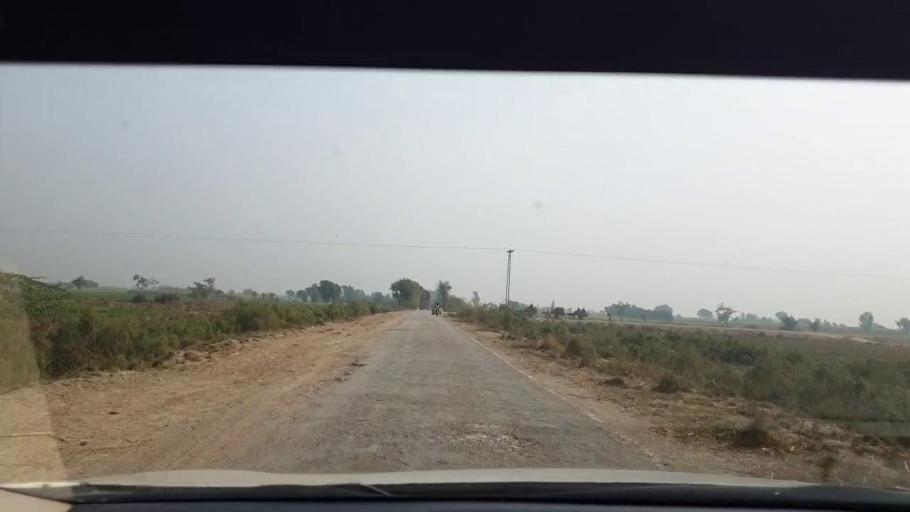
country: PK
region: Sindh
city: Berani
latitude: 25.8473
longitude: 68.8257
